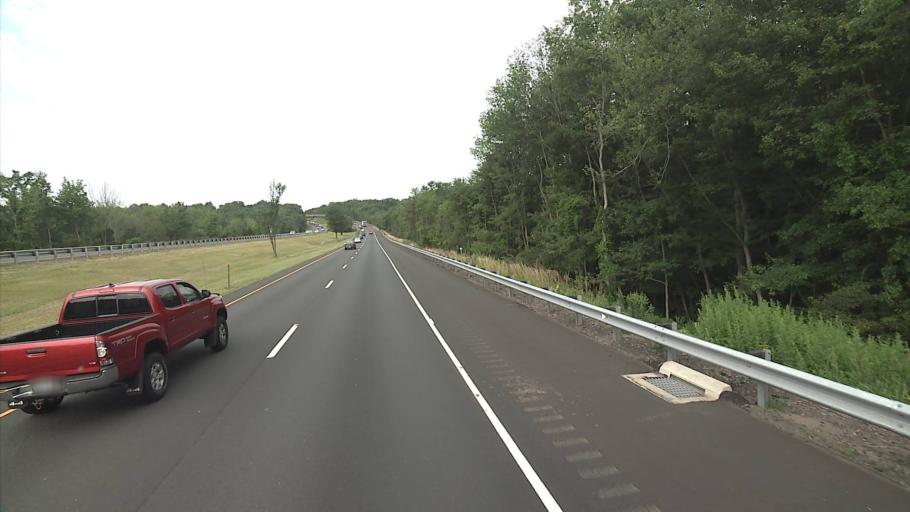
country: US
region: Connecticut
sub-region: New Haven County
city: Middlebury
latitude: 41.5102
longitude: -73.1344
